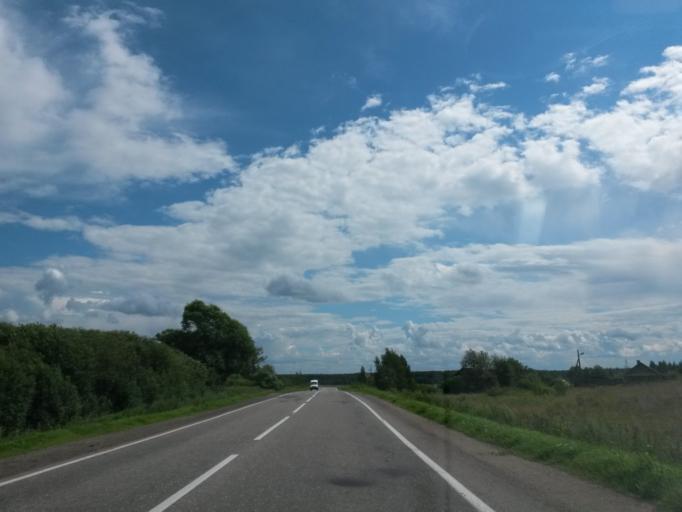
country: RU
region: Jaroslavl
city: Gavrilov-Yam
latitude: 57.3057
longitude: 39.9411
